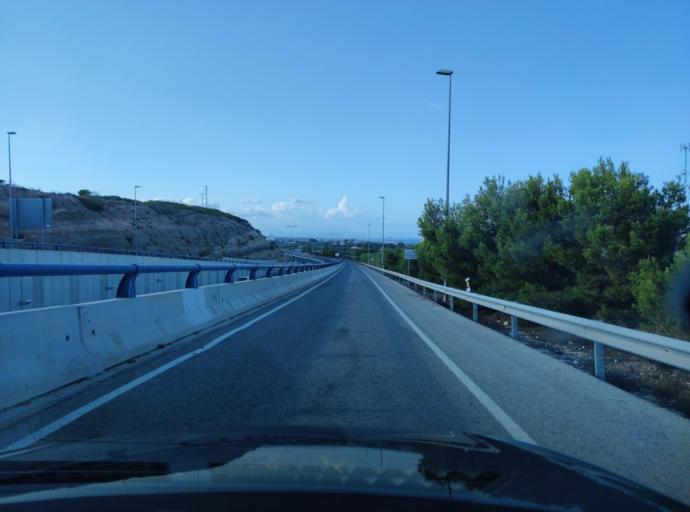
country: ES
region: Valencia
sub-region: Provincia de Alicante
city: Guardamar del Segura
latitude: 38.0629
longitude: -0.6559
